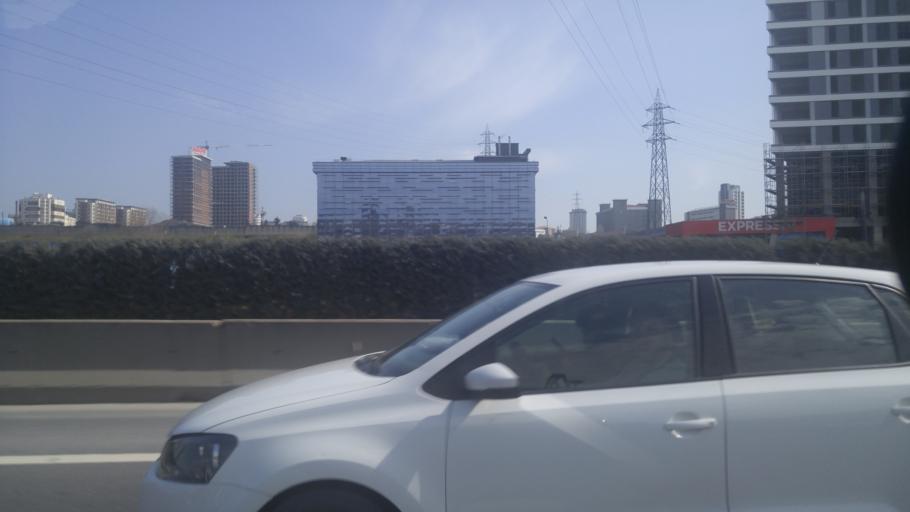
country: TR
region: Istanbul
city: Mahmutbey
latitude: 41.0562
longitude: 28.8105
